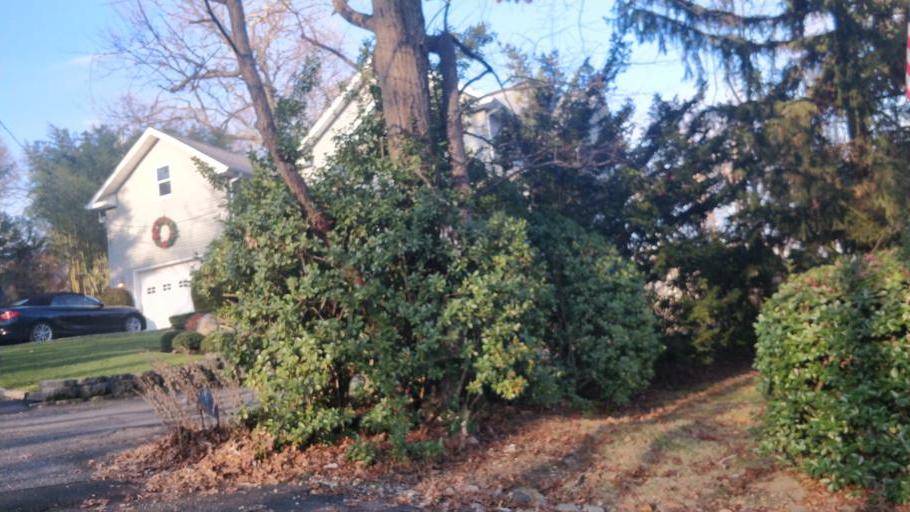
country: US
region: New York
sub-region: Nassau County
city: Bayville
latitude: 40.9078
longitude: -73.5633
